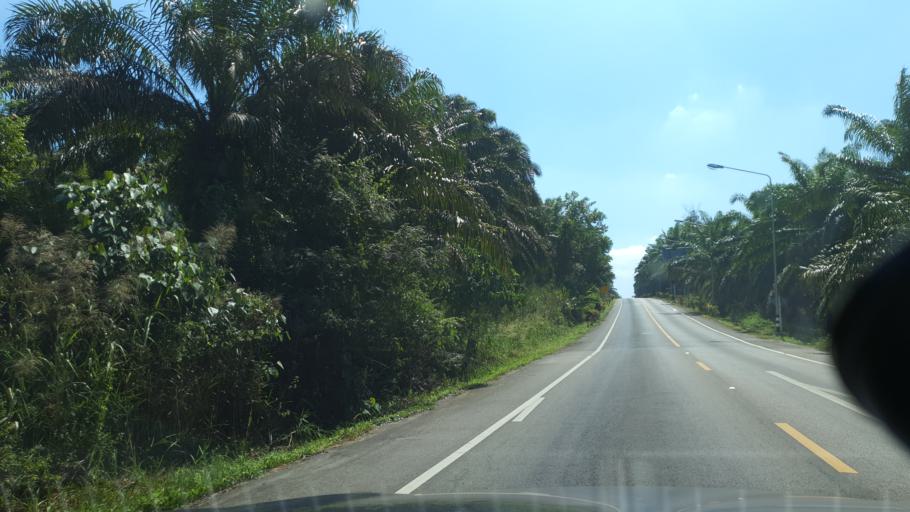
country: TH
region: Krabi
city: Khlong Thom
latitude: 7.9460
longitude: 99.2153
